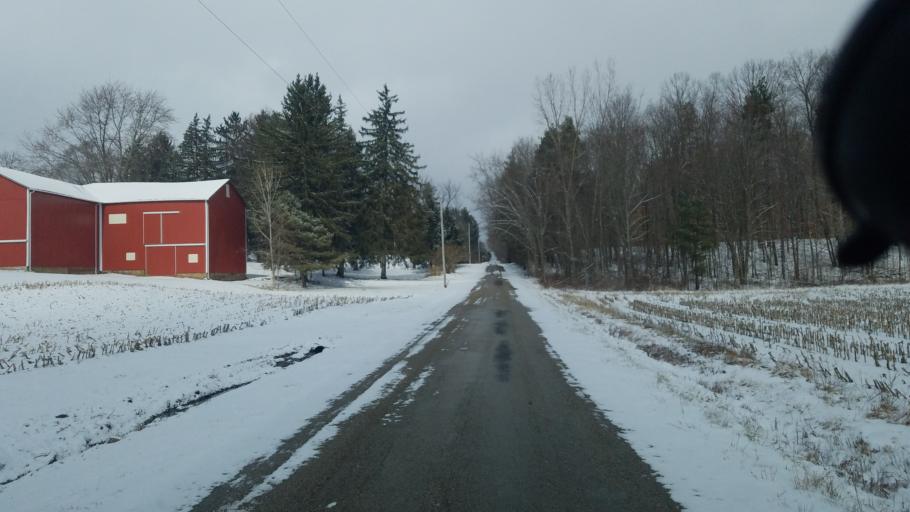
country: US
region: Ohio
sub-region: Richland County
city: Lexington
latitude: 40.6638
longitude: -82.6449
